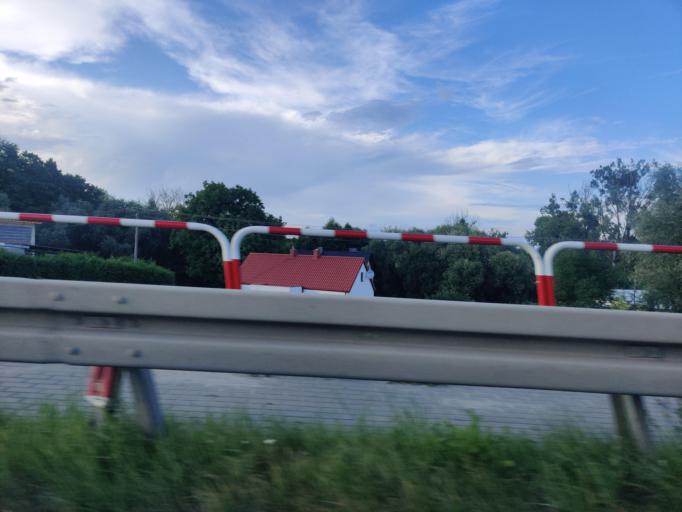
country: PL
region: Greater Poland Voivodeship
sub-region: Konin
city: Konin
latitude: 52.1985
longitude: 18.2947
